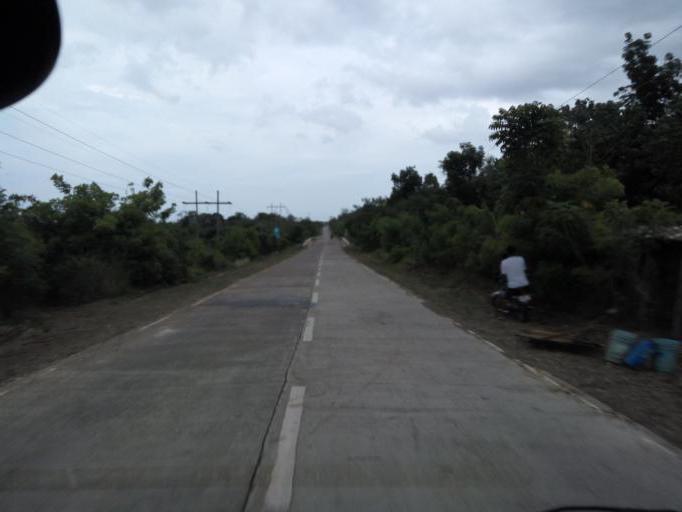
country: PH
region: Cagayan Valley
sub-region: Province of Cagayan
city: Magapit
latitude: 18.1368
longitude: 121.7169
